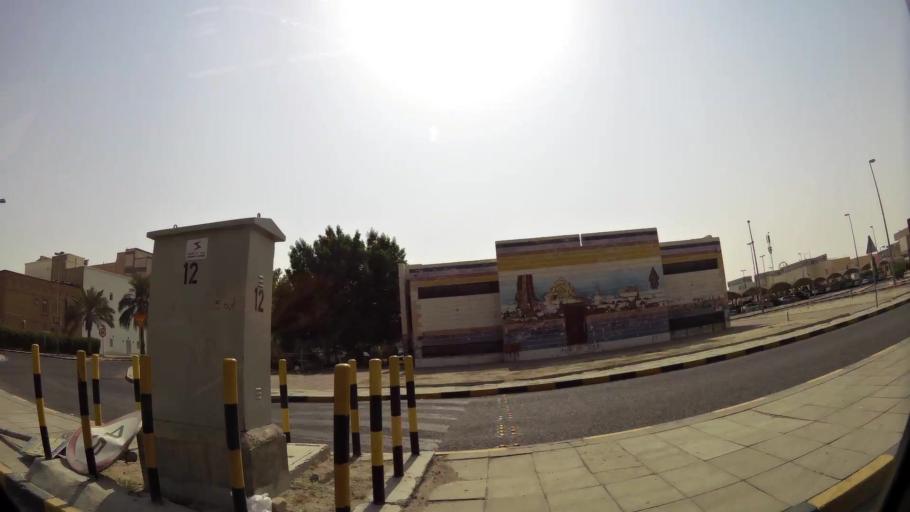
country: KW
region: Muhafazat al Jahra'
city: Al Jahra'
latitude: 29.3248
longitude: 47.6713
